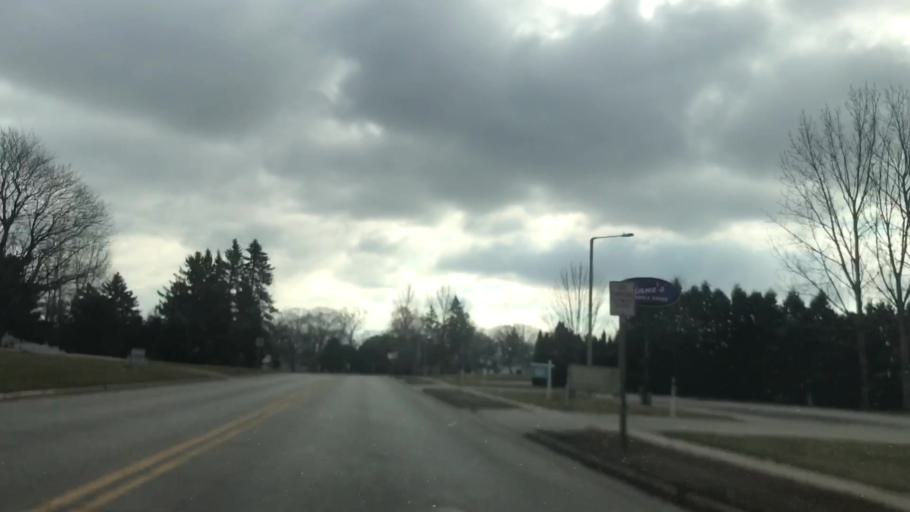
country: US
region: Wisconsin
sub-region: Dodge County
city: Horicon
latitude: 43.4480
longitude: -88.6199
